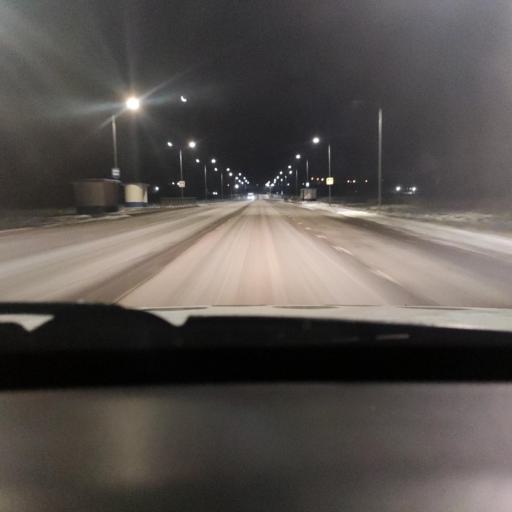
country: RU
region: Perm
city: Kultayevo
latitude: 57.8718
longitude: 55.8651
